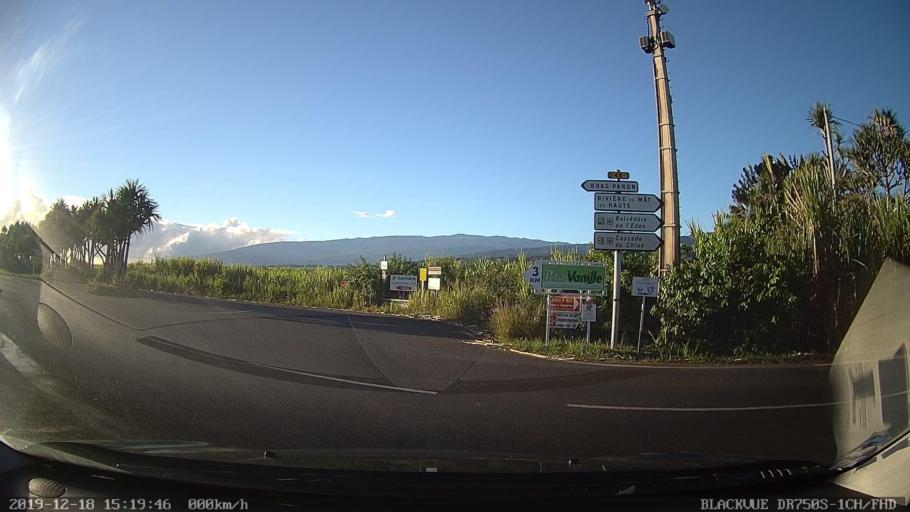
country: RE
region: Reunion
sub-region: Reunion
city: Bras-Panon
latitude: -20.9900
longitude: 55.6611
